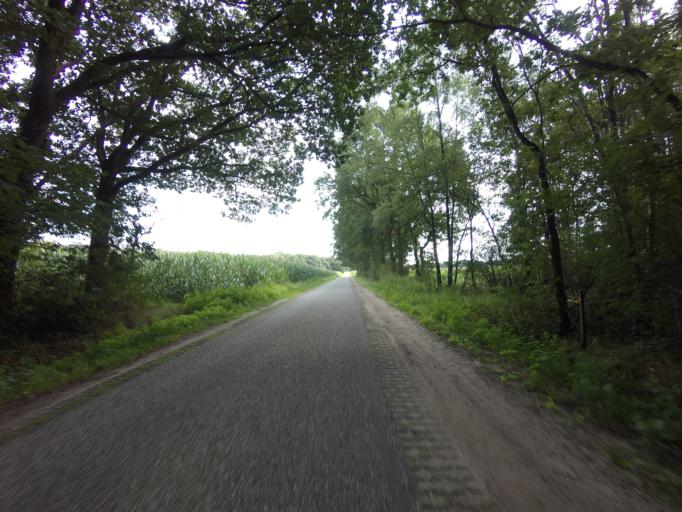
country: NL
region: Overijssel
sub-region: Gemeente Tubbergen
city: Tubbergen
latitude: 52.4133
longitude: 6.8353
